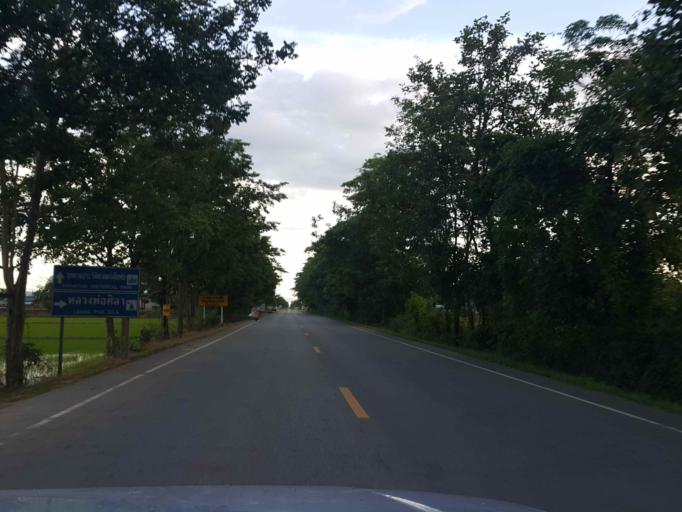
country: TH
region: Sukhothai
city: Sawankhalok
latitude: 17.3123
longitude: 99.7337
